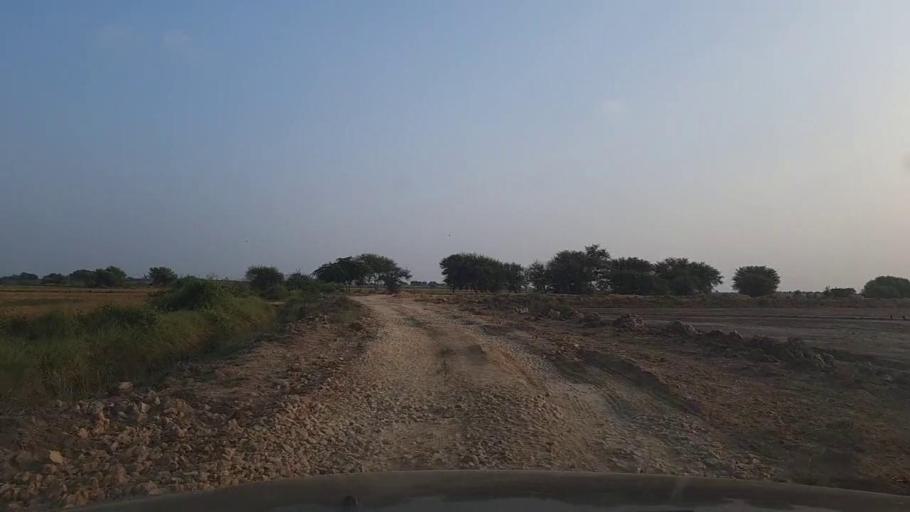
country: PK
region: Sindh
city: Jati
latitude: 24.5379
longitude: 68.3605
